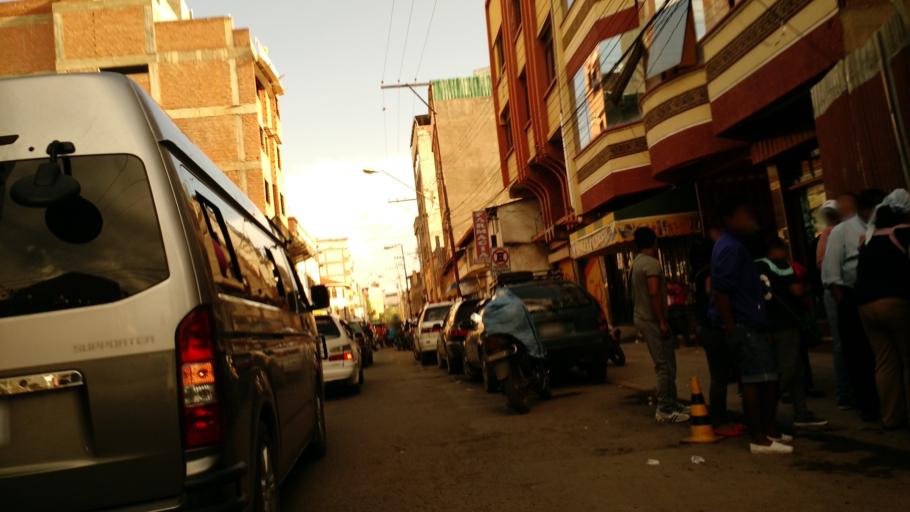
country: BO
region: Cochabamba
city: Cochabamba
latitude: -17.3997
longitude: -66.1564
